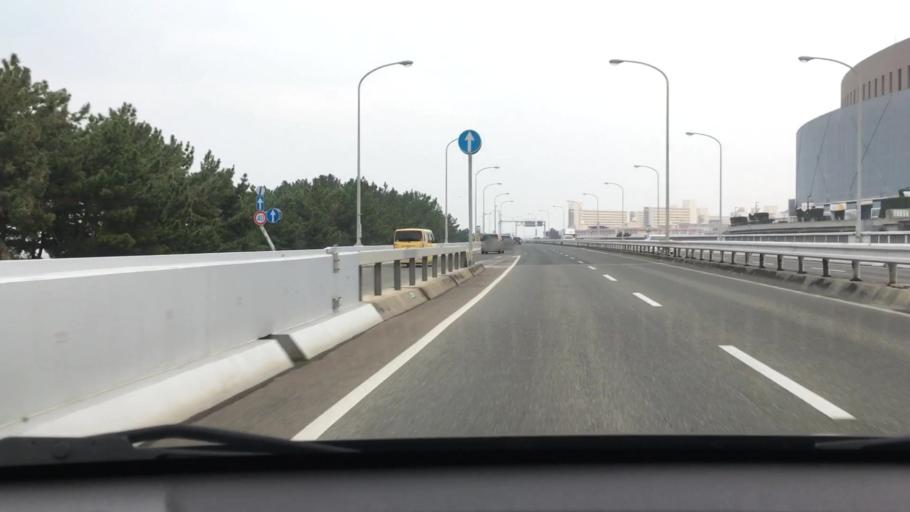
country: JP
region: Fukuoka
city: Fukuoka-shi
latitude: 33.5960
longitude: 130.3594
